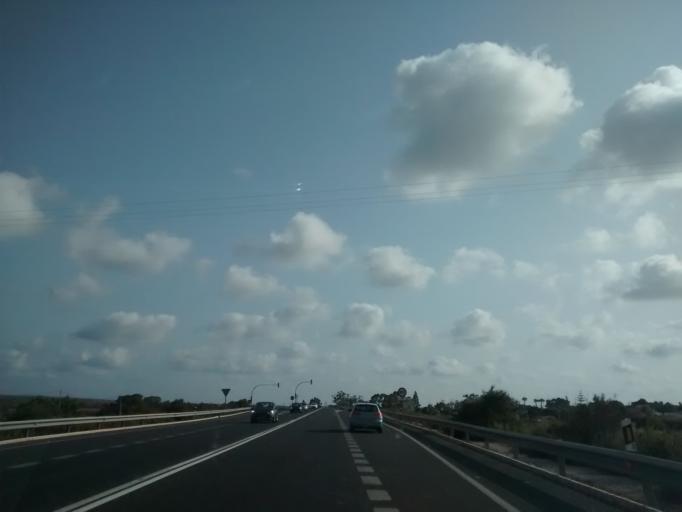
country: ES
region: Valencia
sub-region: Provincia de Alicante
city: Santa Pola
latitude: 38.2627
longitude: -0.5441
